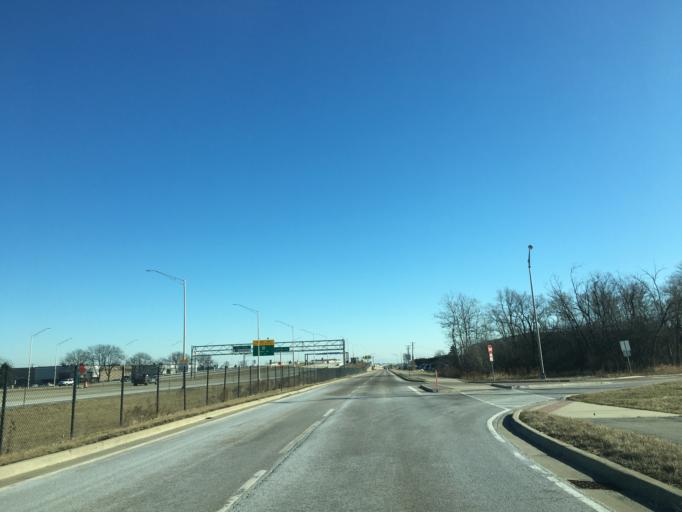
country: US
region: Illinois
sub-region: DuPage County
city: Wood Dale
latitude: 41.9830
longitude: -87.9763
